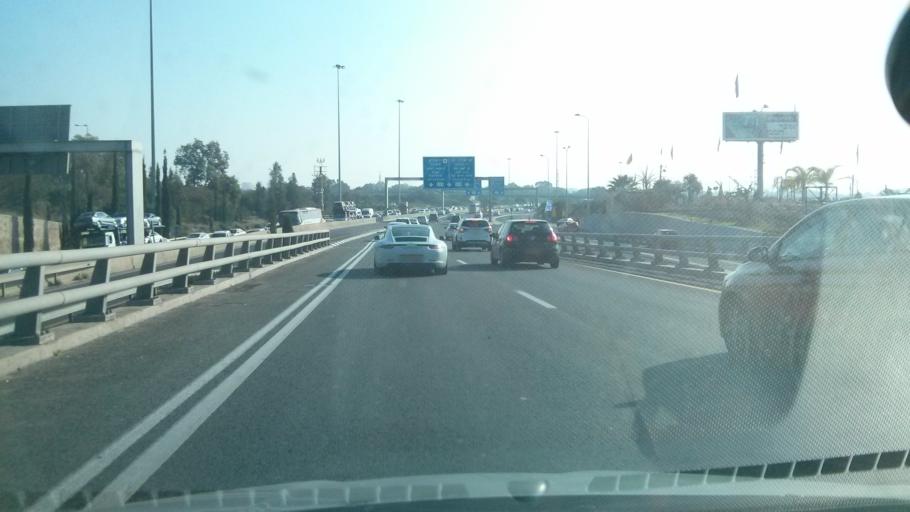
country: IL
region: Tel Aviv
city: Herzliya Pituah
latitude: 32.1402
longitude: 34.8036
